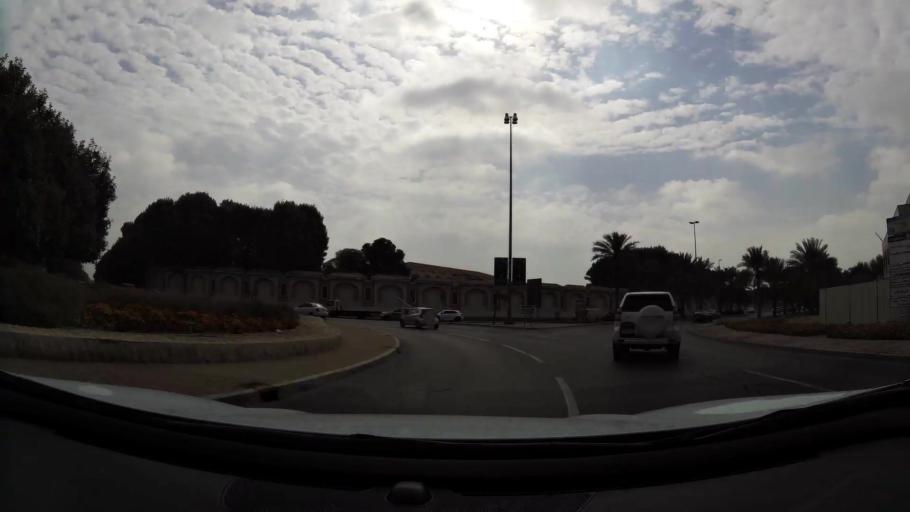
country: AE
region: Abu Dhabi
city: Al Ain
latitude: 24.2239
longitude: 55.7507
